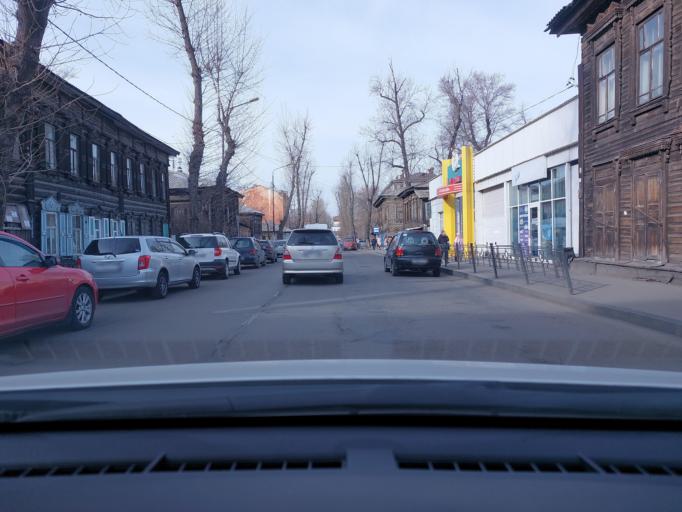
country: RU
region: Irkutsk
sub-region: Irkutskiy Rayon
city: Irkutsk
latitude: 52.2810
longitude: 104.2907
